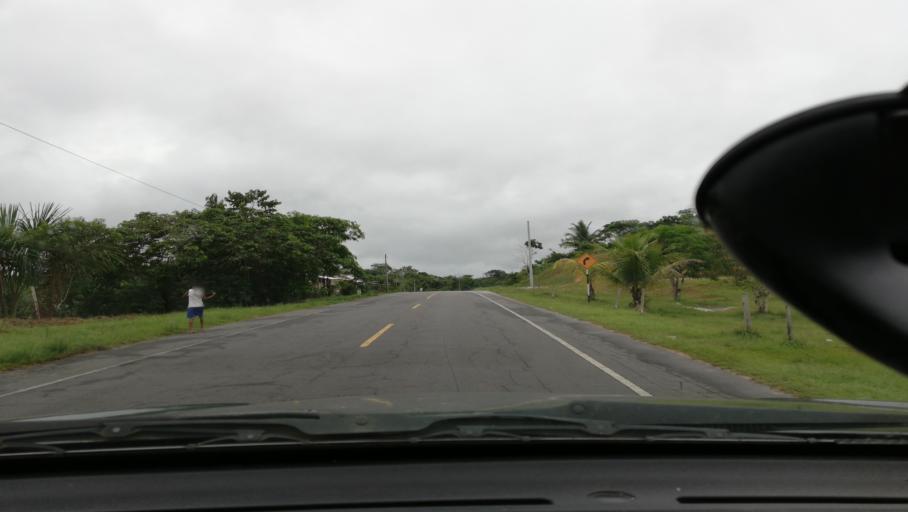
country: PE
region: Loreto
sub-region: Provincia de Loreto
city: Nauta
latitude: -4.3572
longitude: -73.5530
